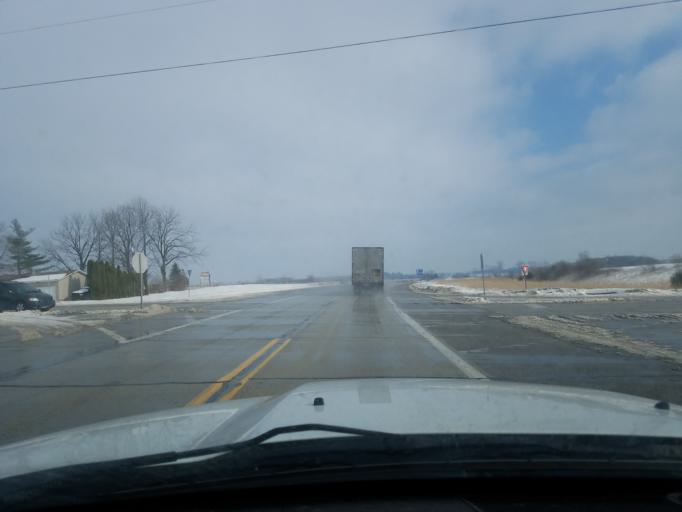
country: US
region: Indiana
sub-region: Marshall County
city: Bremen
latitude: 41.4605
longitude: -86.1926
